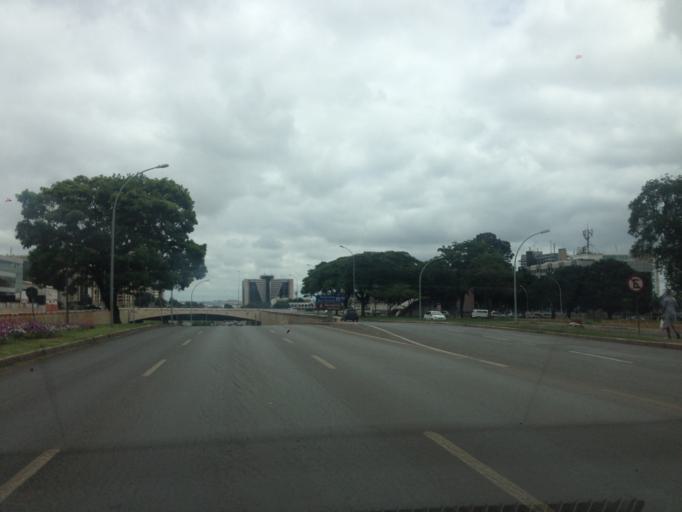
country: BR
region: Federal District
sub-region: Brasilia
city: Brasilia
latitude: -15.7949
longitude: -47.8905
